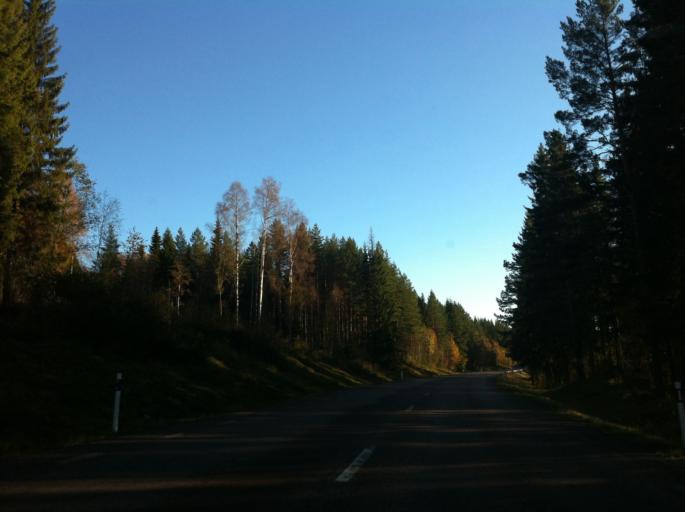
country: SE
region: Dalarna
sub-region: Faluns Kommun
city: Bjursas
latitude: 60.7776
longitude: 15.3157
